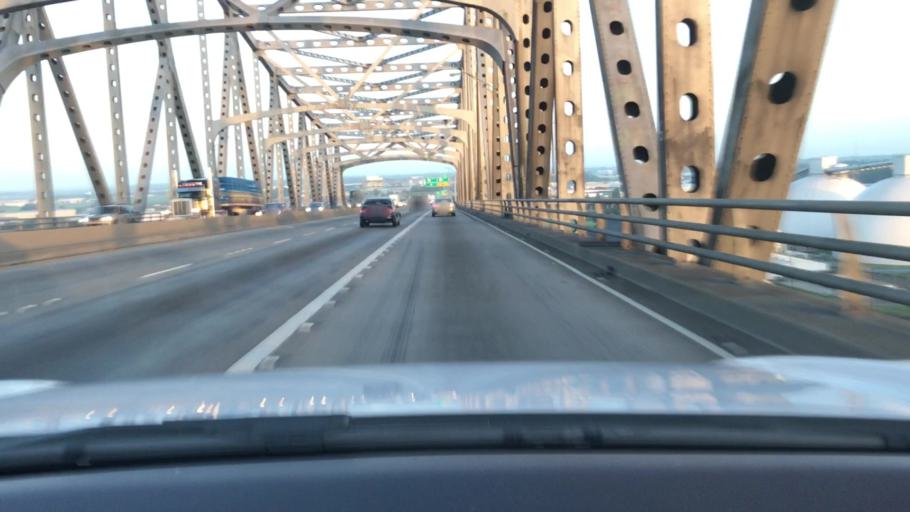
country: US
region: Louisiana
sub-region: West Baton Rouge Parish
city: Port Allen
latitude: 30.4399
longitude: -91.1999
